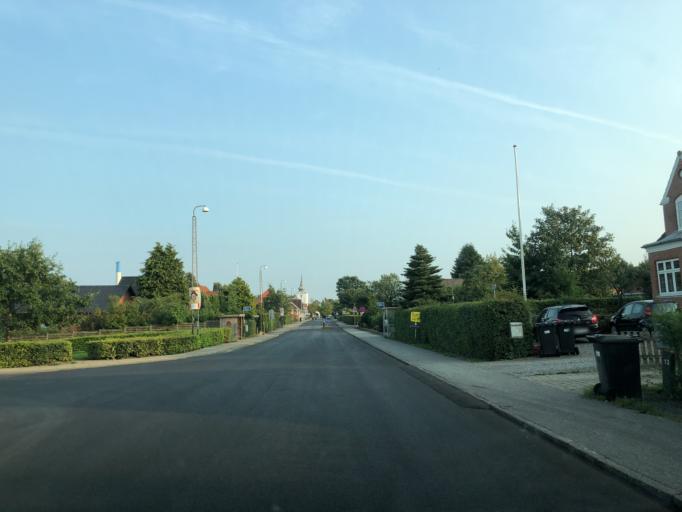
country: DK
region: South Denmark
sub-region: Vejle Kommune
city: Jelling
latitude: 55.7050
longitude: 9.3780
